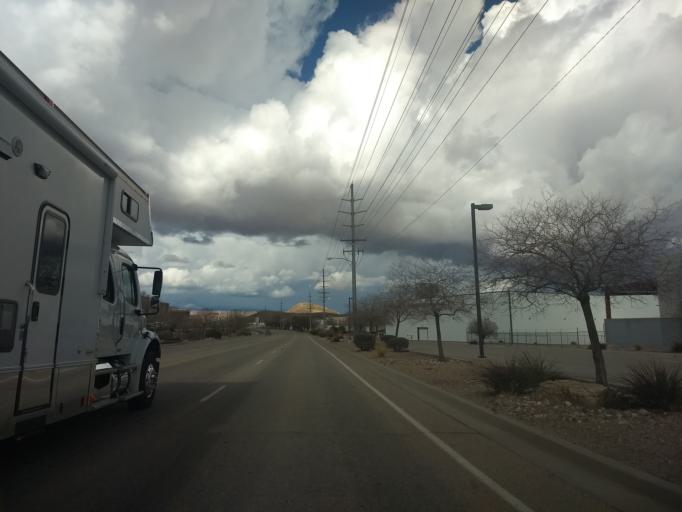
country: US
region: Utah
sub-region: Washington County
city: Saint George
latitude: 37.0395
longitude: -113.5571
